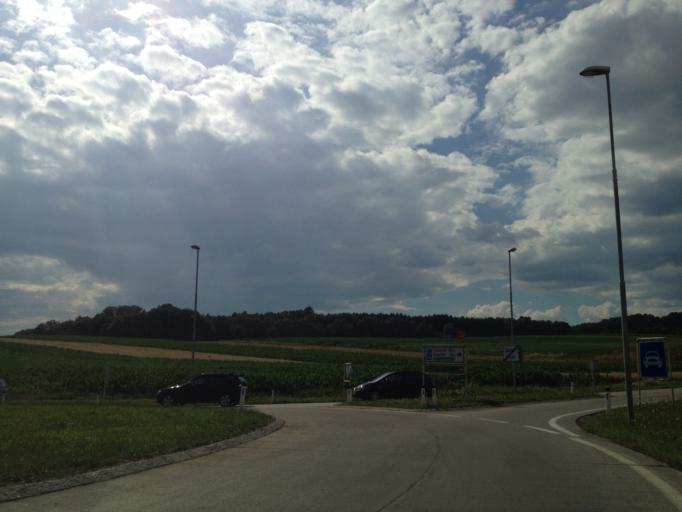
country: AT
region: Burgenland
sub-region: Politischer Bezirk Oberwart
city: Oberwart
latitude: 47.2867
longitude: 16.1859
